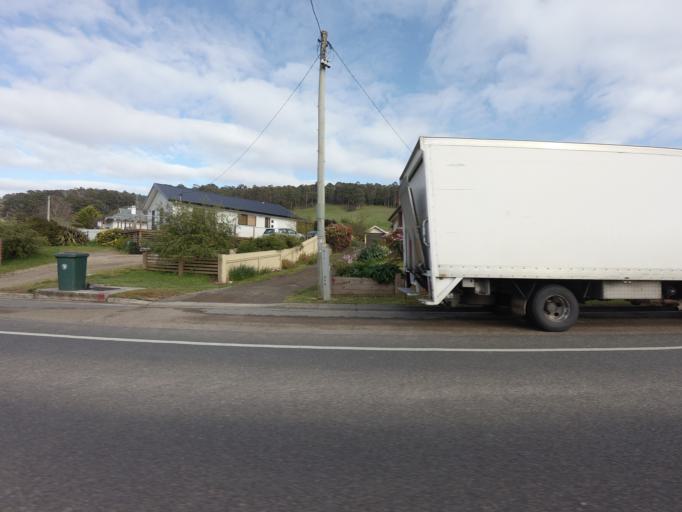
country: AU
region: Tasmania
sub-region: Huon Valley
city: Huonville
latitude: -43.0406
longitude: 147.0450
